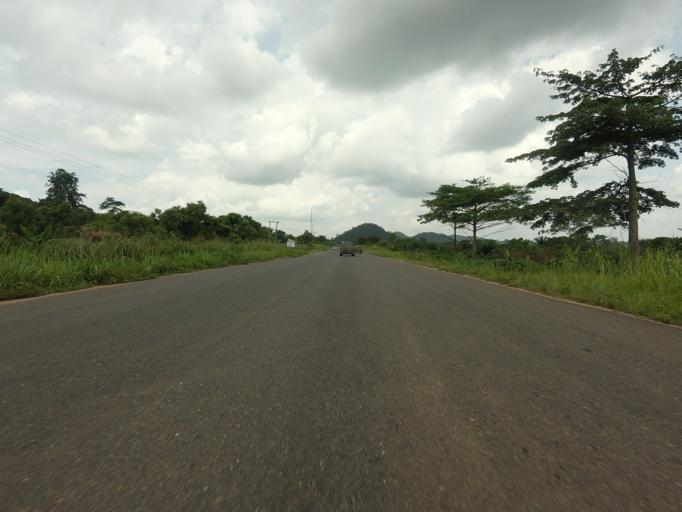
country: GH
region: Volta
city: Ho
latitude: 6.4353
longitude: 0.1707
